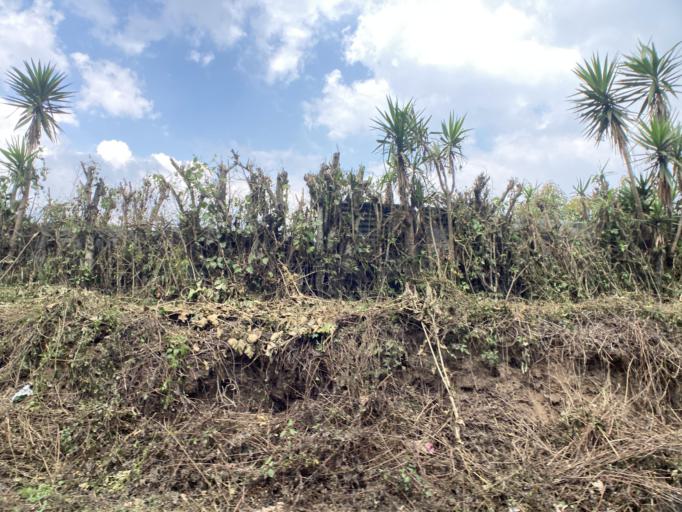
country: GT
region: Guatemala
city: Villa Canales
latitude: 14.4113
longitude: -90.5350
